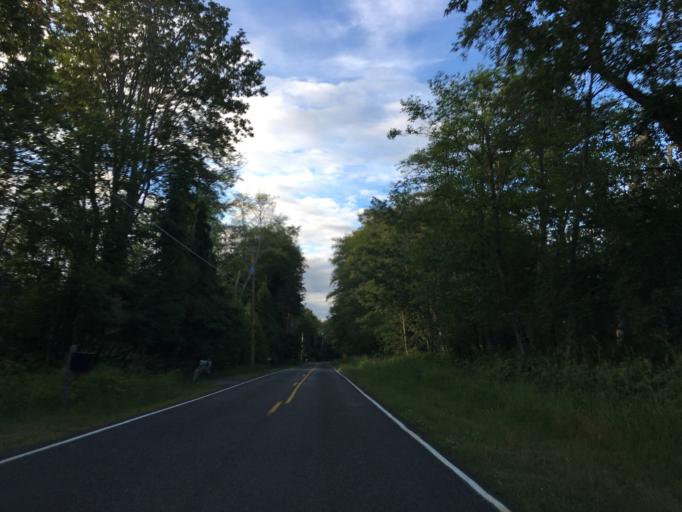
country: CA
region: British Columbia
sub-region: Greater Vancouver Regional District
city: White Rock
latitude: 48.9535
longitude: -122.8164
